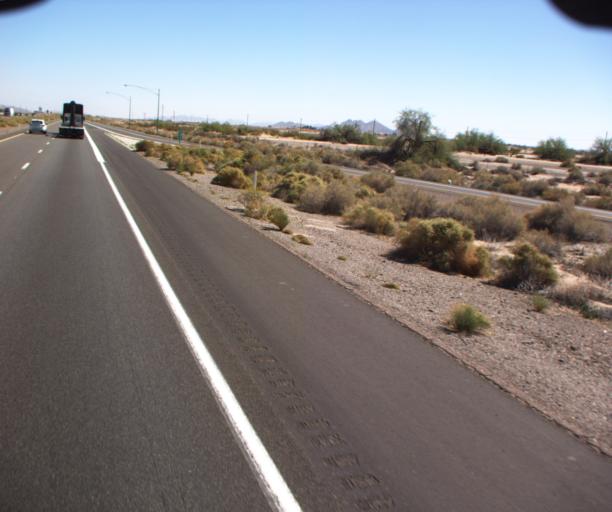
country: US
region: Arizona
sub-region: Yuma County
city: Wellton
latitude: 32.6623
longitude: -114.1397
